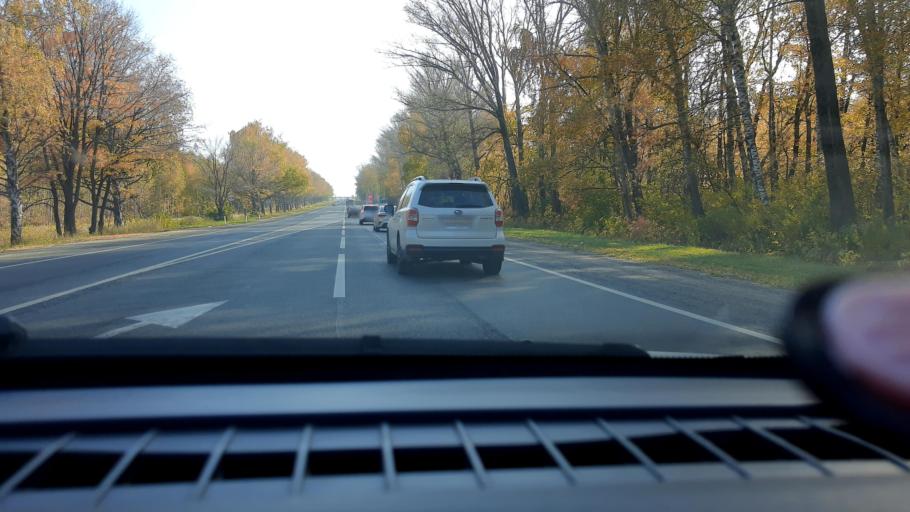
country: RU
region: Nizjnij Novgorod
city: Kstovo
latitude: 56.1389
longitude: 44.2333
